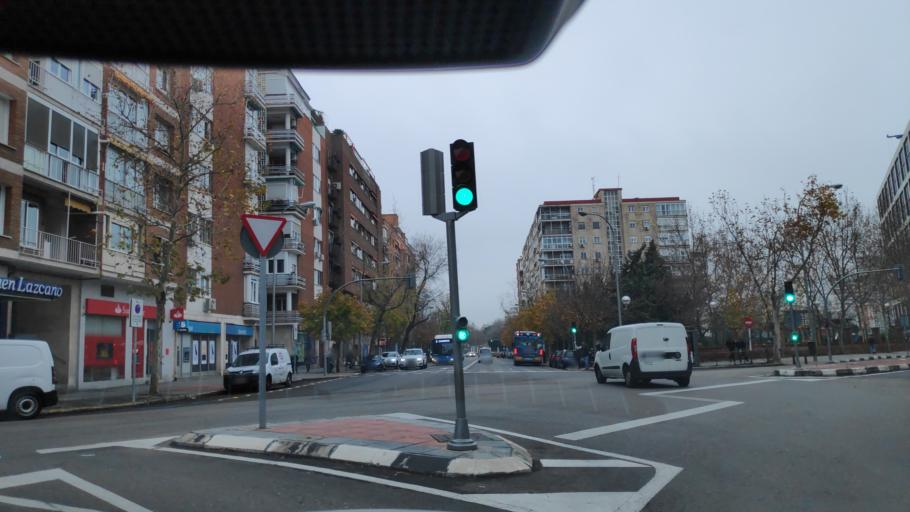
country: ES
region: Madrid
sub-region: Provincia de Madrid
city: Chamartin
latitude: 40.4689
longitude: -3.6870
